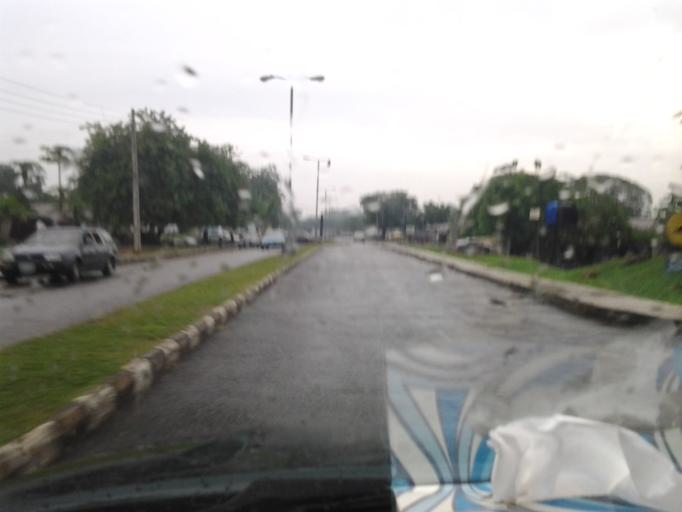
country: NG
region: Oyo
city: Ibadan
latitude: 7.4529
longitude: 3.8990
